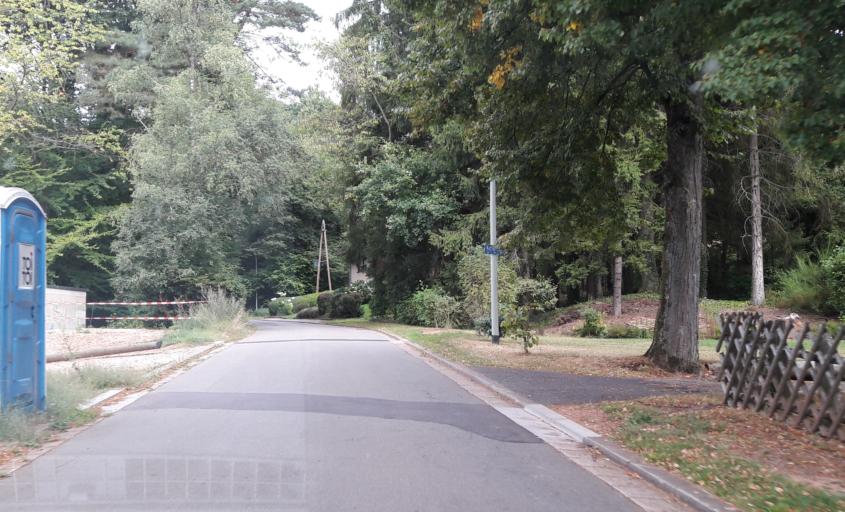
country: DE
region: Saarland
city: Oberthal
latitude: 49.5181
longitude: 7.0877
